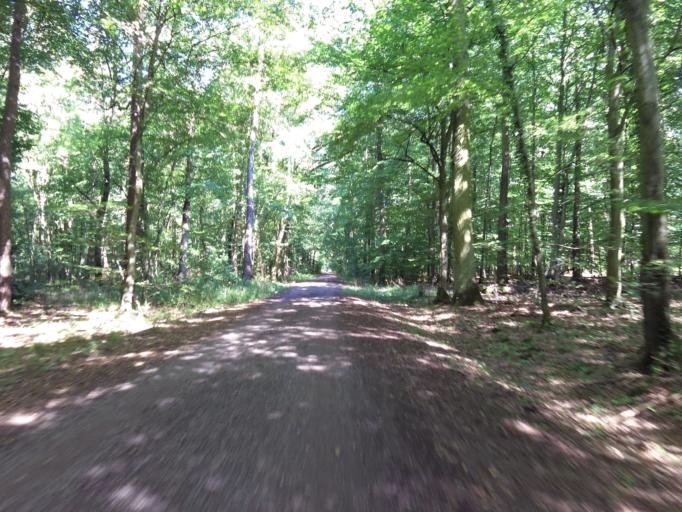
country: DE
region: Rheinland-Pfalz
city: Harthausen
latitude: 49.2964
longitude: 8.3294
